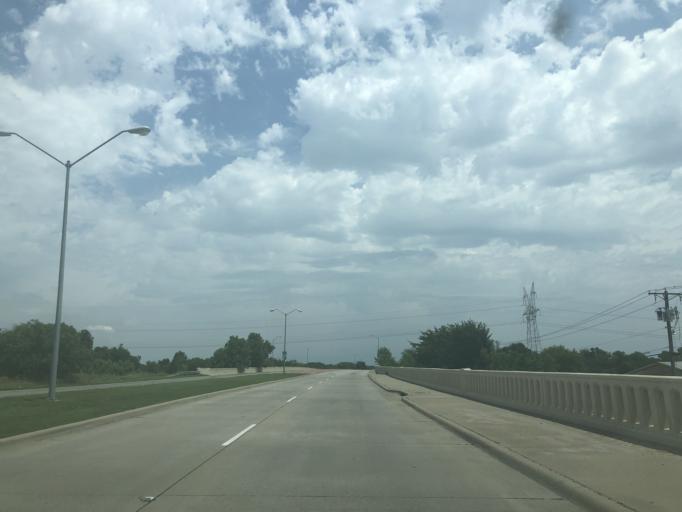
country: US
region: Texas
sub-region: Dallas County
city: Irving
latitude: 32.7775
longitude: -96.9601
